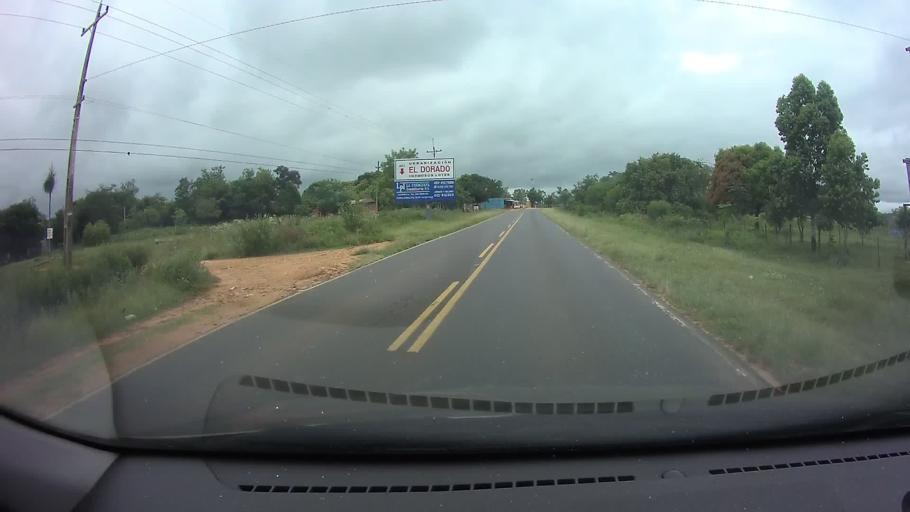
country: PY
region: Central
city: Guarambare
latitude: -25.5170
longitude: -57.4903
